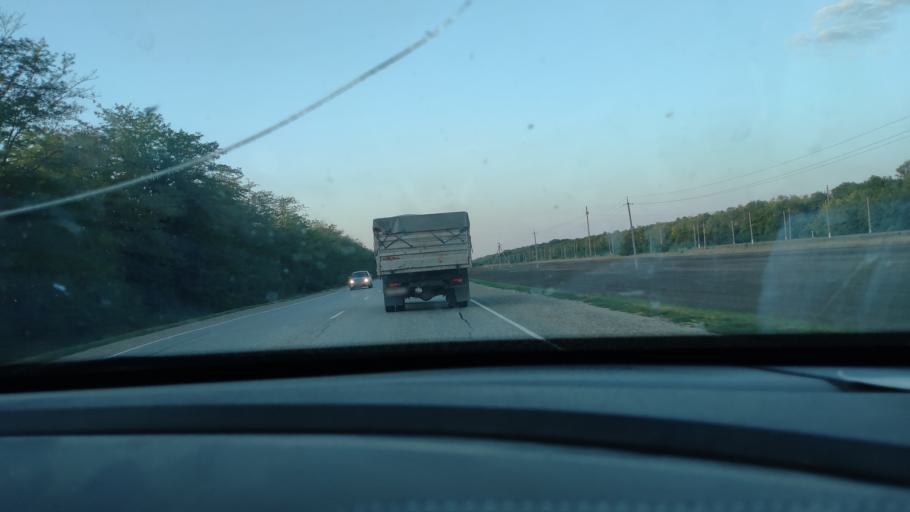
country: RU
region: Krasnodarskiy
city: Starominskaya
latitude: 46.4783
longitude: 39.0497
